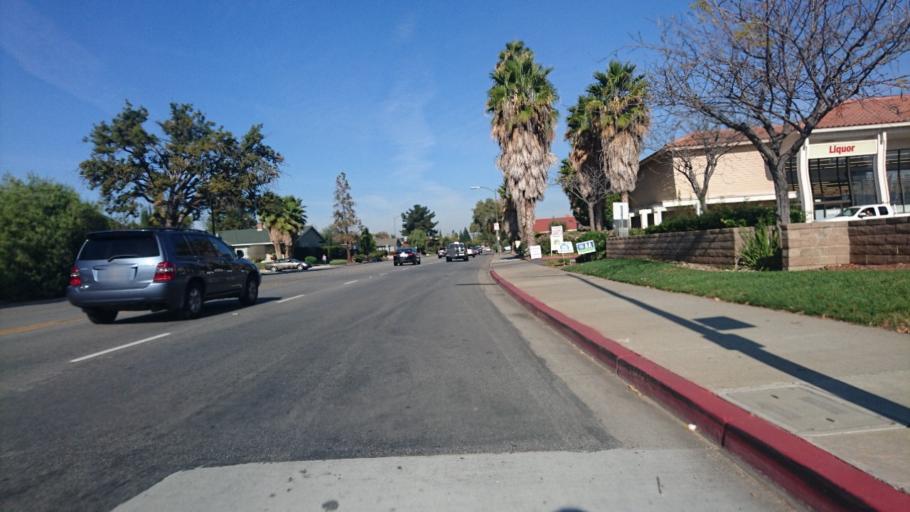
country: US
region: California
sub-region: Santa Clara County
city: Cambrian Park
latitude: 37.2565
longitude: -121.8991
